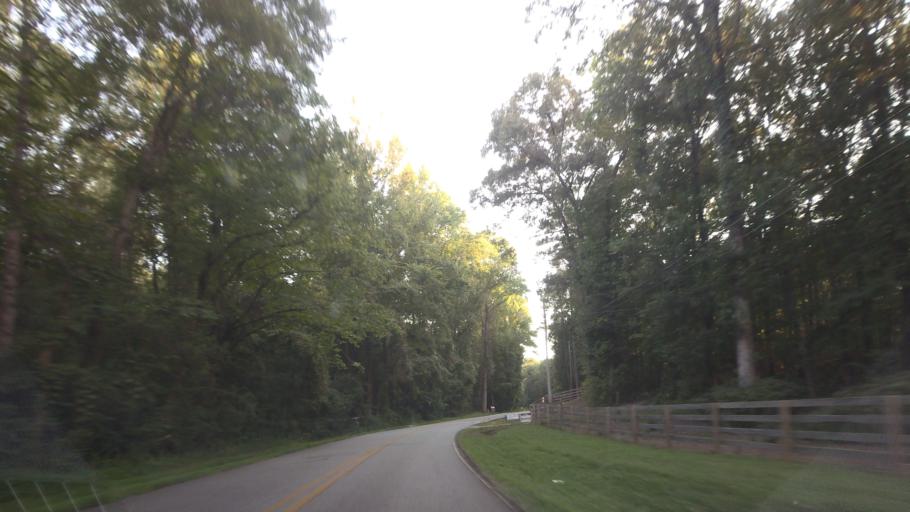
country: US
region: Georgia
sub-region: Bibb County
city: West Point
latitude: 32.9256
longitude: -83.8084
